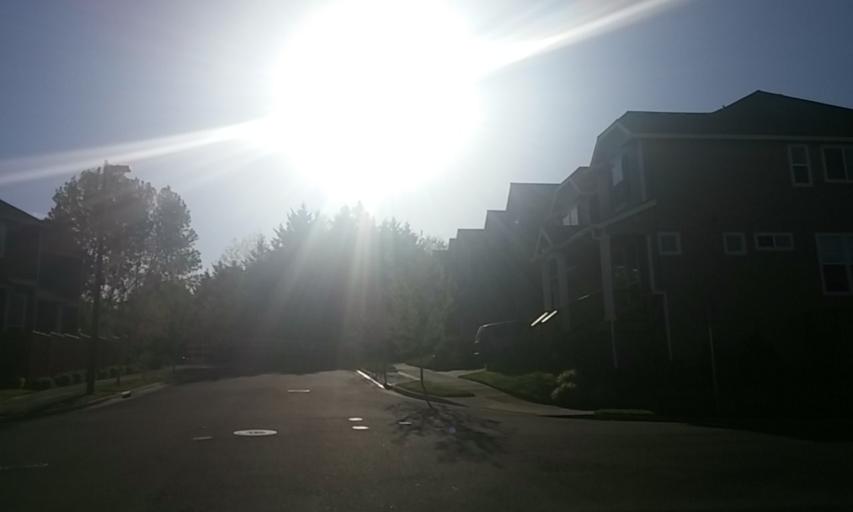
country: US
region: Oregon
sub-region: Washington County
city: Cedar Mill
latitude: 45.5463
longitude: -122.7946
